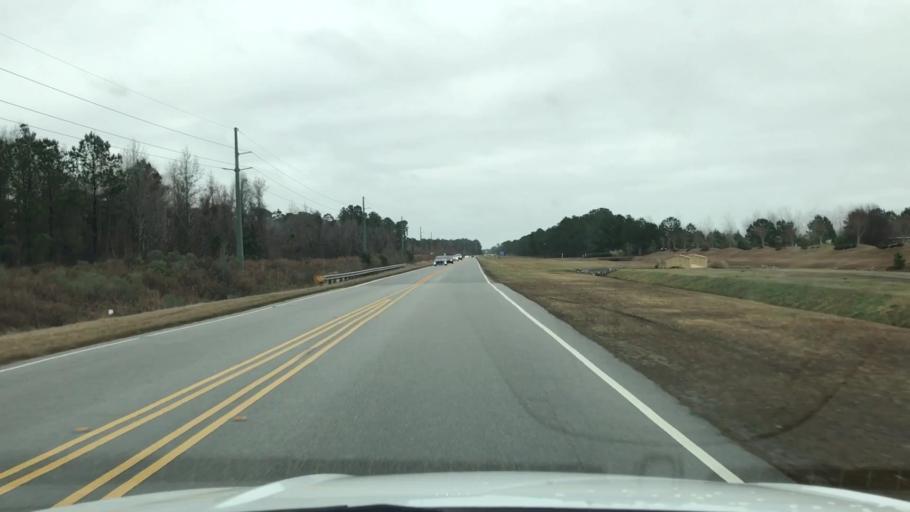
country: US
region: South Carolina
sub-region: Horry County
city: Myrtle Beach
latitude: 33.7378
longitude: -78.8947
